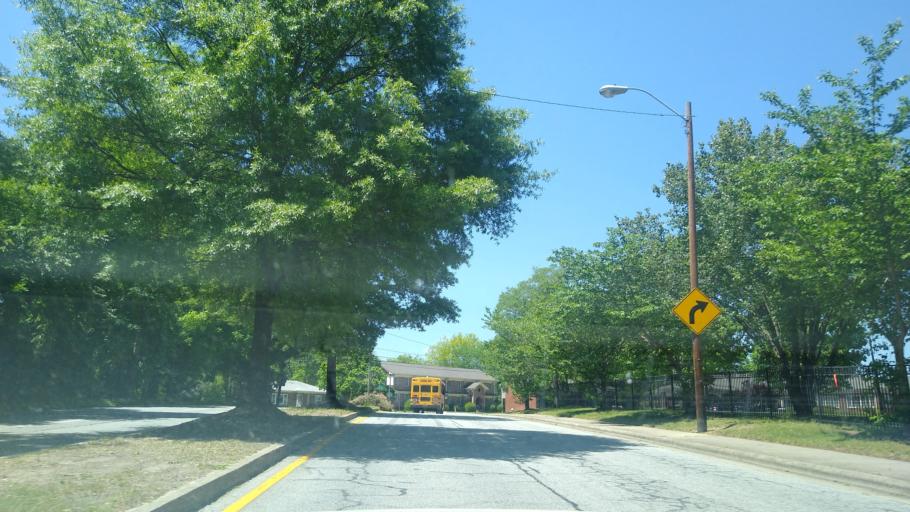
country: US
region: North Carolina
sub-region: Guilford County
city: Greensboro
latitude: 36.0829
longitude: -79.7820
